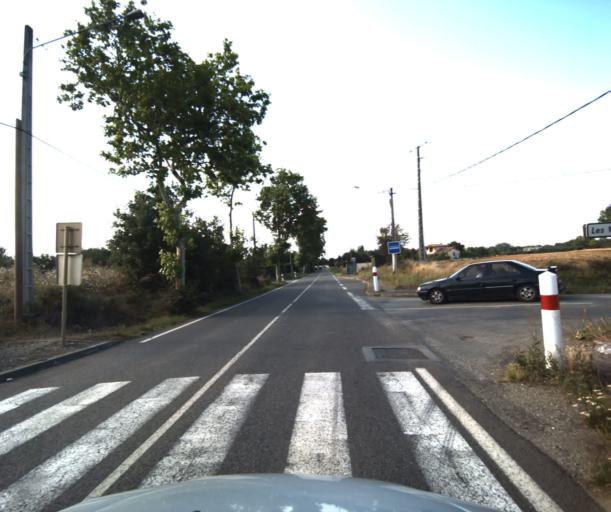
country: FR
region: Midi-Pyrenees
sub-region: Departement de la Haute-Garonne
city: Muret
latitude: 43.4430
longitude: 1.3391
